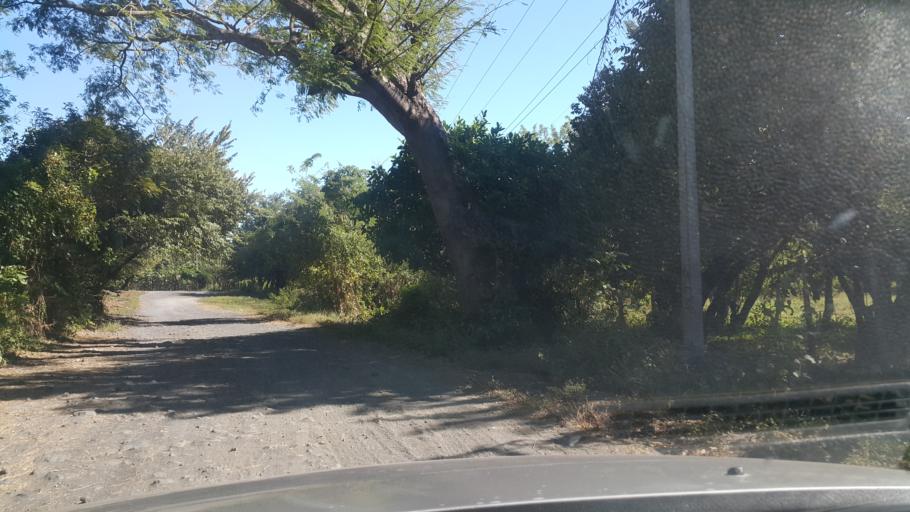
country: NI
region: Rivas
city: Altagracia
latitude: 11.4915
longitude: -85.6173
